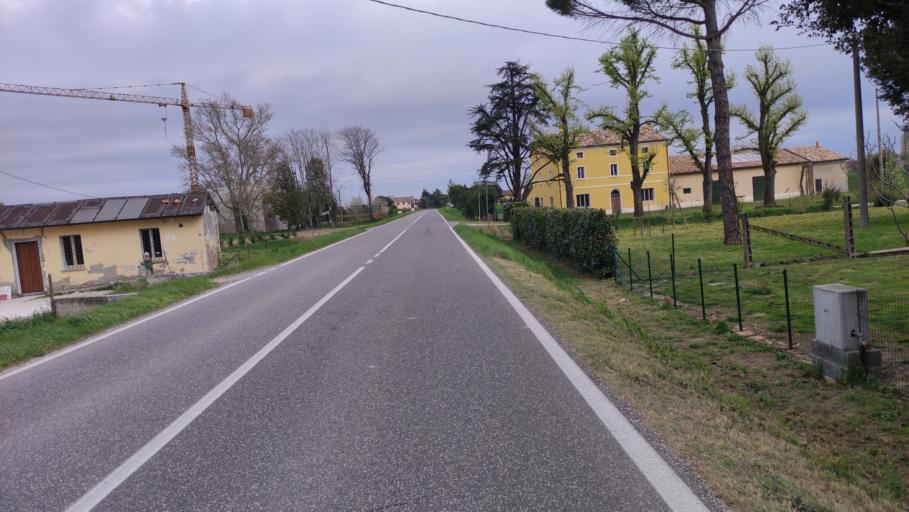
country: IT
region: Emilia-Romagna
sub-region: Provincia di Ravenna
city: Godo
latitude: 44.3923
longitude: 12.0537
